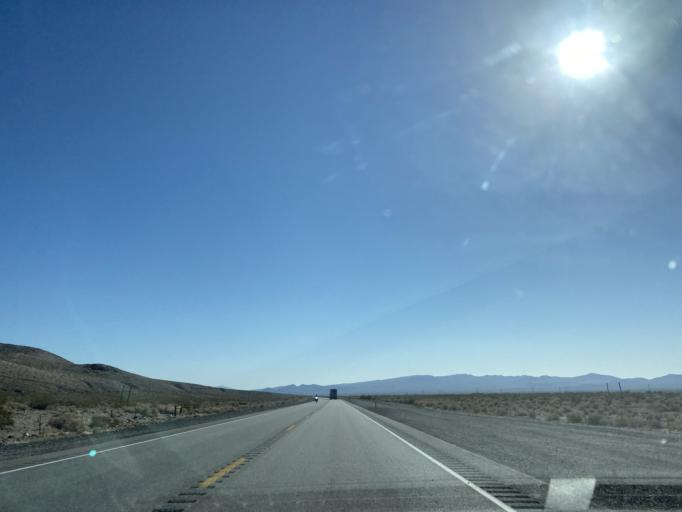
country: US
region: Nevada
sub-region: Nye County
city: Beatty
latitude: 36.8787
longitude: -116.7533
